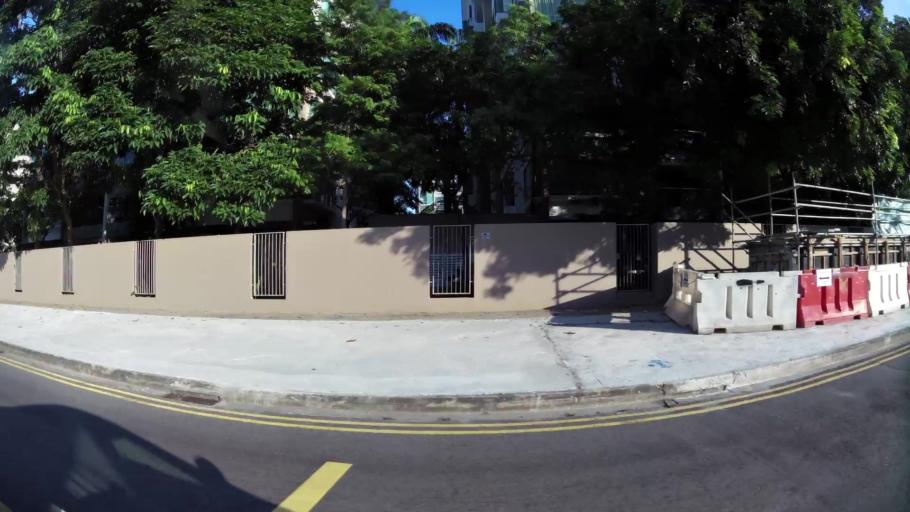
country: SG
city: Singapore
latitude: 1.3072
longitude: 103.9163
